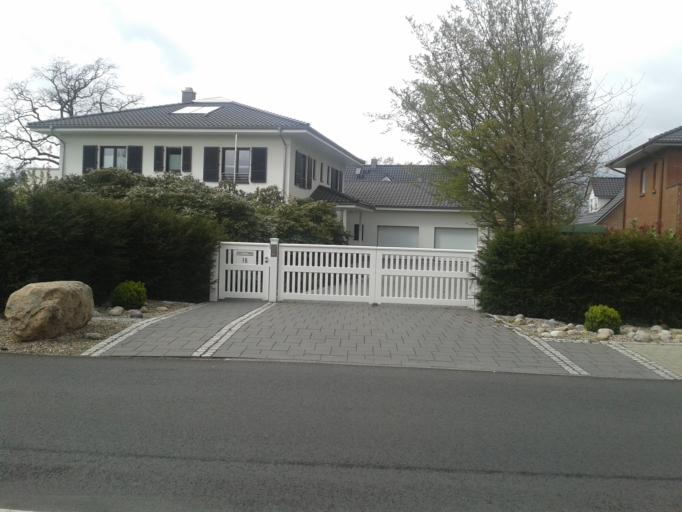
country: DE
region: Schleswig-Holstein
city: Halstenbek
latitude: 53.6030
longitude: 9.8146
